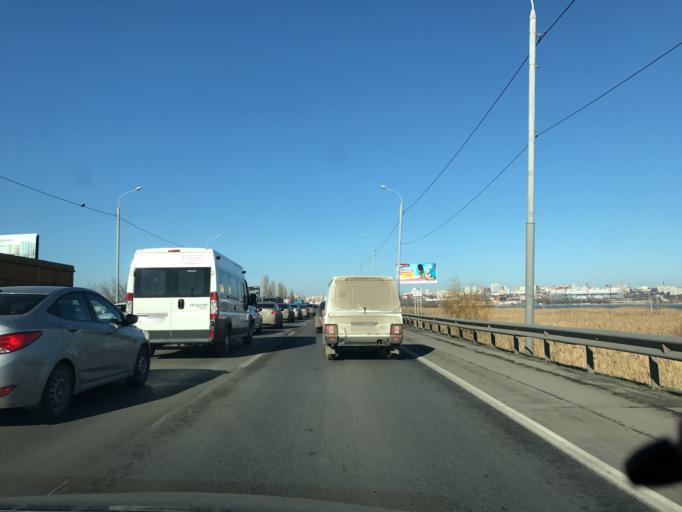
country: RU
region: Rostov
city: Rostov-na-Donu
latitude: 47.1884
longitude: 39.7358
